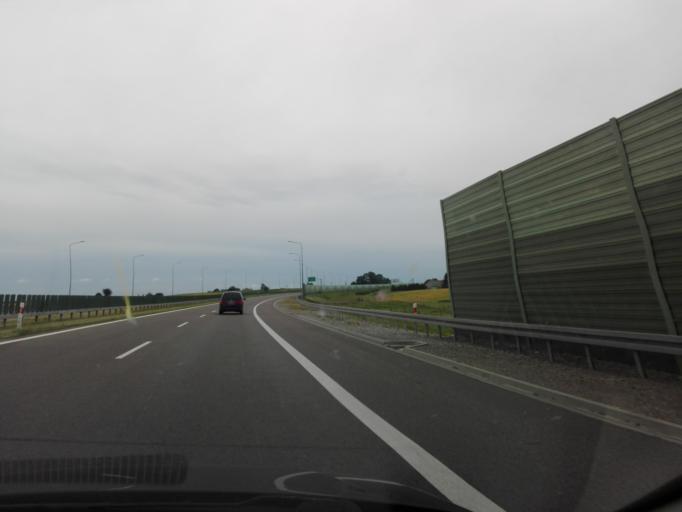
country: PL
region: Lublin Voivodeship
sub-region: Powiat lubelski
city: Jastkow
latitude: 51.3381
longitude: 22.3871
